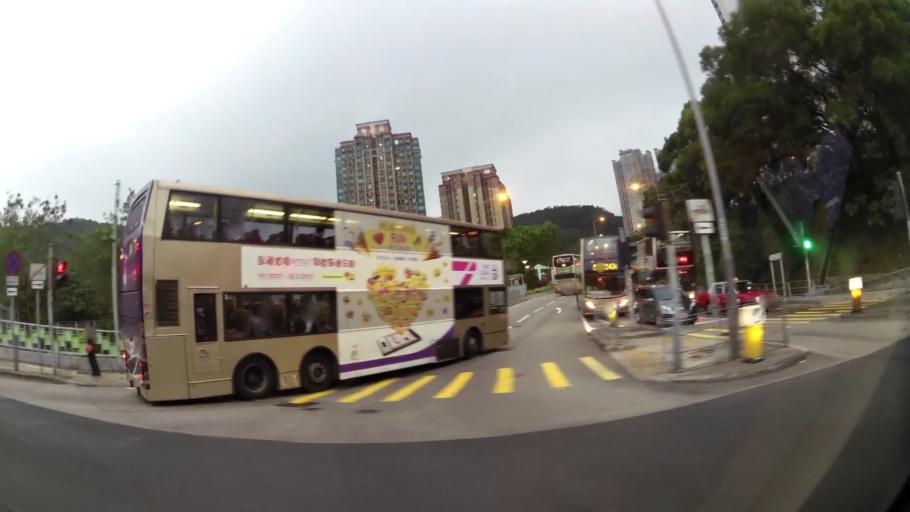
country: HK
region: Tsuen Wan
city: Tsuen Wan
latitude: 22.3525
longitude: 114.0984
